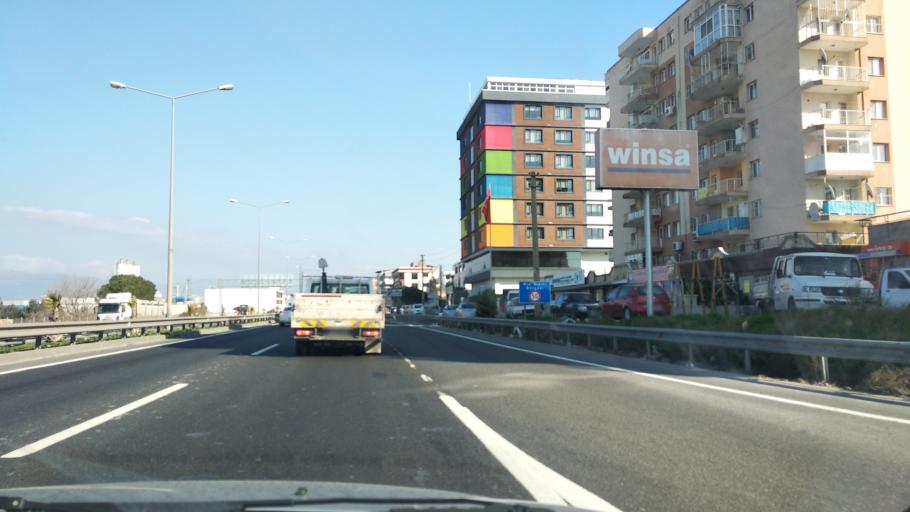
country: TR
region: Izmir
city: Menemen
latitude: 38.5722
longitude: 27.0588
